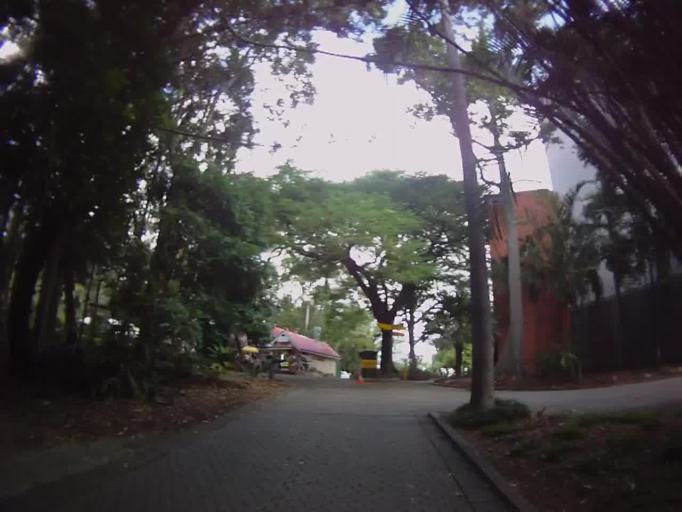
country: AU
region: Queensland
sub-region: Brisbane
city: Brisbane
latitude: -27.4771
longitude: 153.0304
